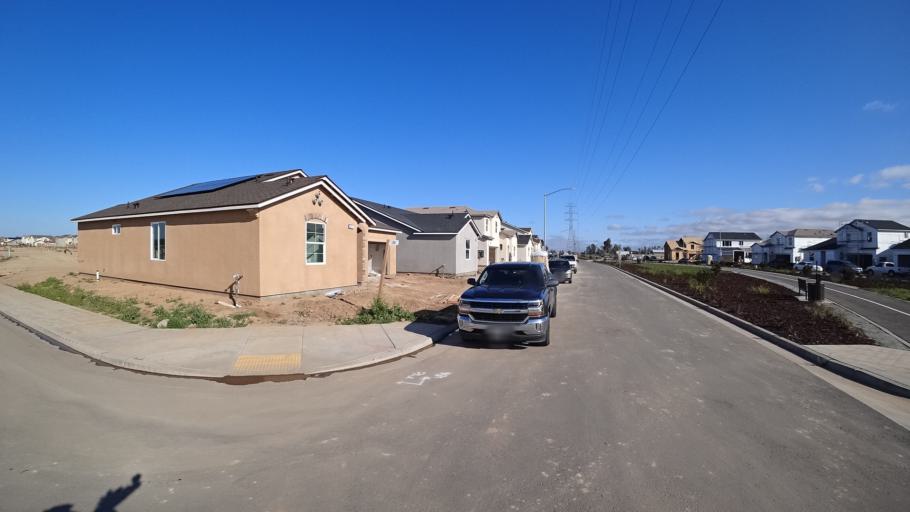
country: US
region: California
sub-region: Fresno County
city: West Park
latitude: 36.7982
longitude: -119.9004
